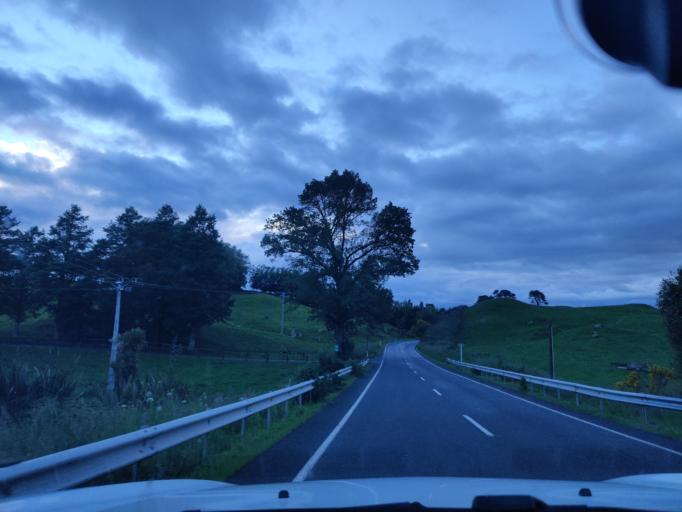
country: NZ
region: Waikato
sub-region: South Waikato District
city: Tokoroa
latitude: -38.1899
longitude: 175.7982
